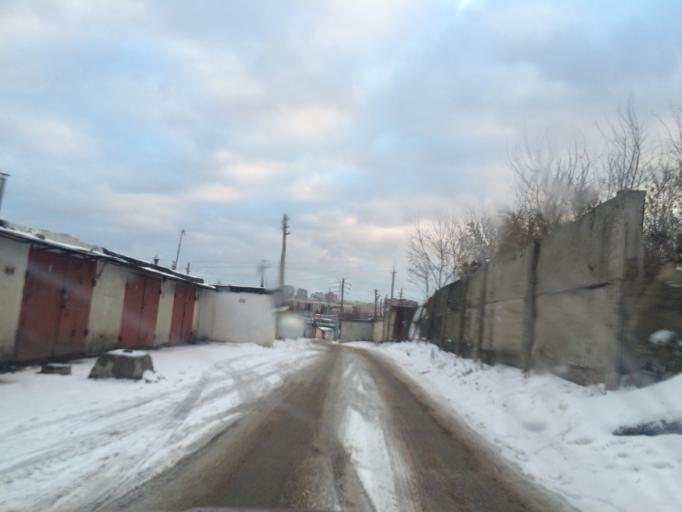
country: RU
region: Tula
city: Tula
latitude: 54.2188
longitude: 37.6823
